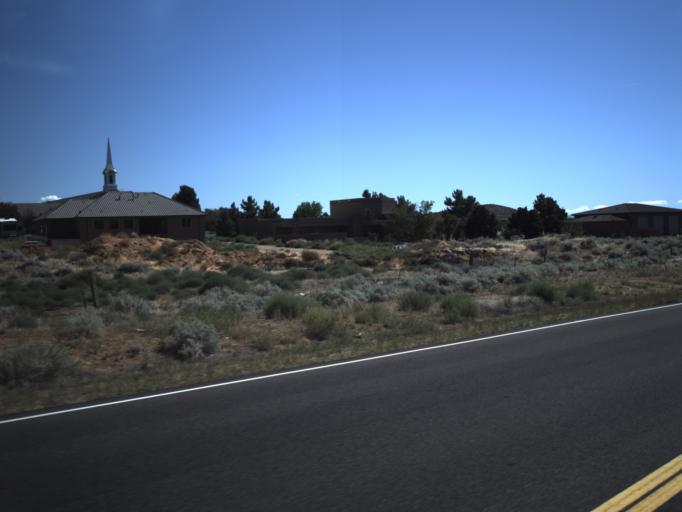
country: US
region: Utah
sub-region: Washington County
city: Ivins
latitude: 37.2021
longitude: -113.6261
